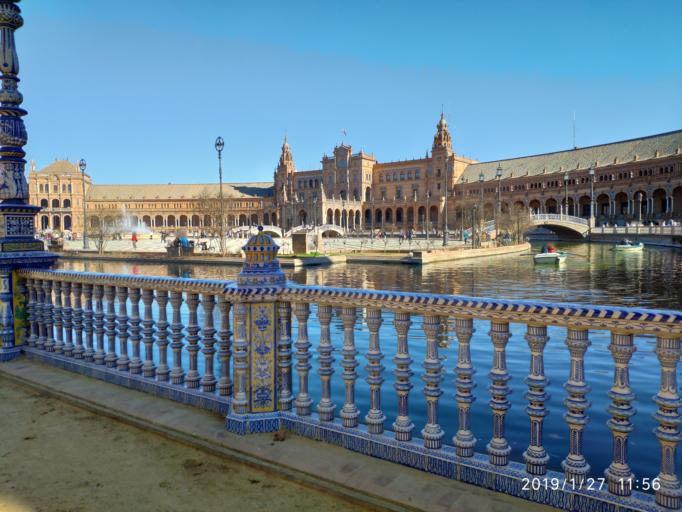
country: ES
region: Andalusia
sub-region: Provincia de Sevilla
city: Sevilla
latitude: 37.3761
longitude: -5.9871
